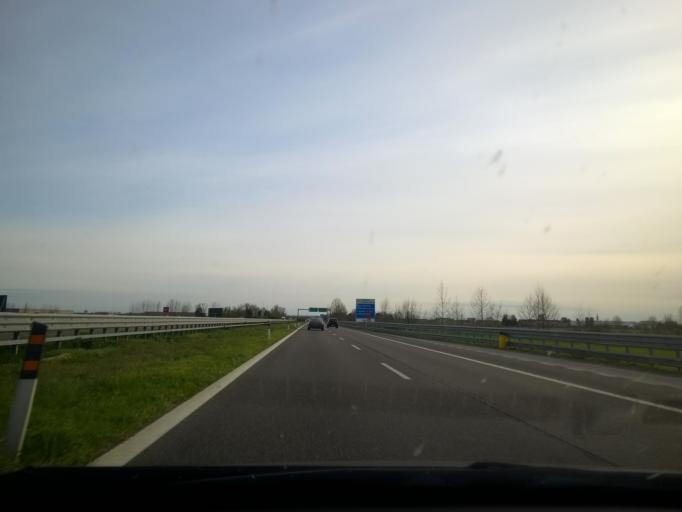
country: IT
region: Lombardy
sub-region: Provincia di Brescia
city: Alfianello
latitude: 45.2786
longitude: 10.1312
